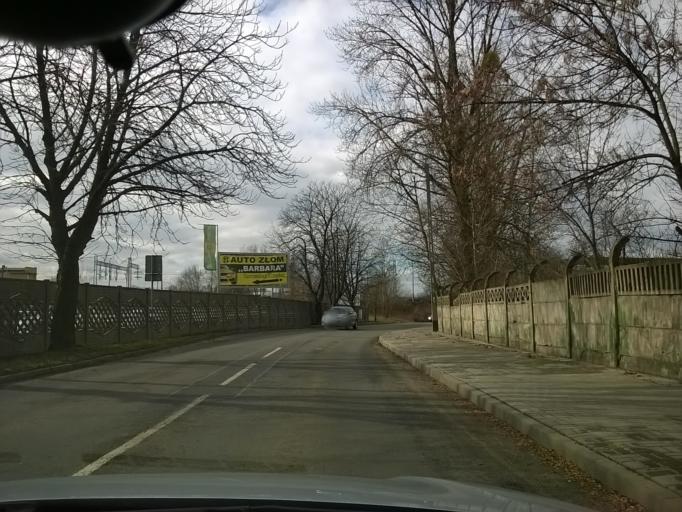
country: PL
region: Silesian Voivodeship
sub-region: Chorzow
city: Chorzow
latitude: 50.3152
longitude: 18.9629
